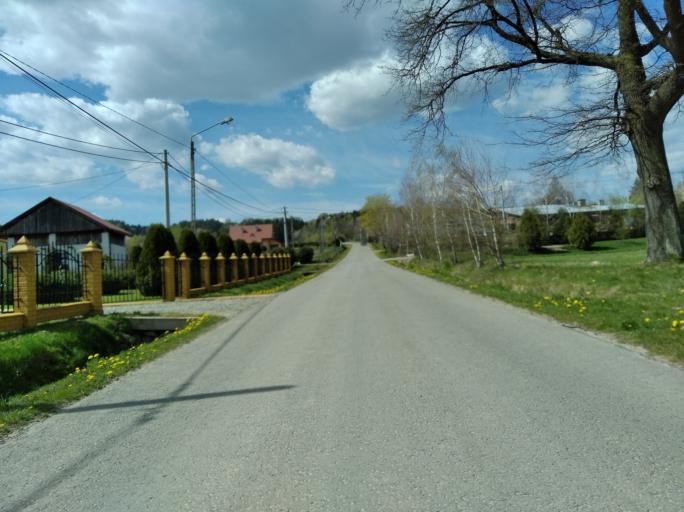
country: PL
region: Subcarpathian Voivodeship
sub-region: Powiat brzozowski
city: Wesola
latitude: 49.7779
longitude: 22.1332
